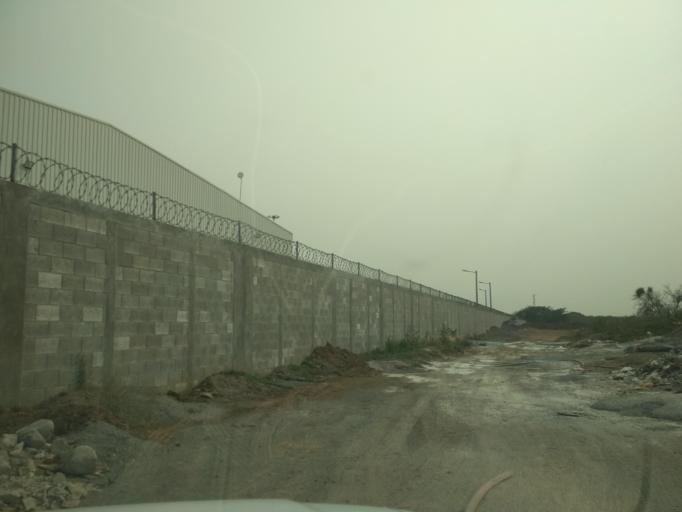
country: MX
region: Veracruz
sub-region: Veracruz
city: Delfino Victoria (Santa Fe)
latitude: 19.1648
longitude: -96.2652
